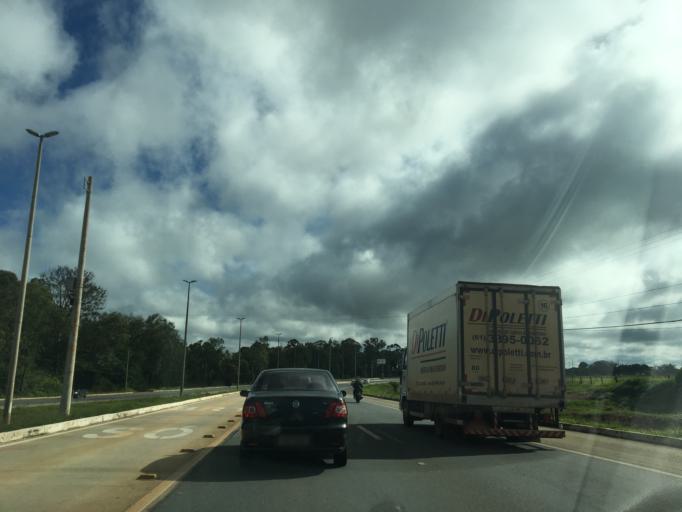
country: BR
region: Federal District
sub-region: Brasilia
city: Brasilia
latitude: -15.9482
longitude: -48.0005
